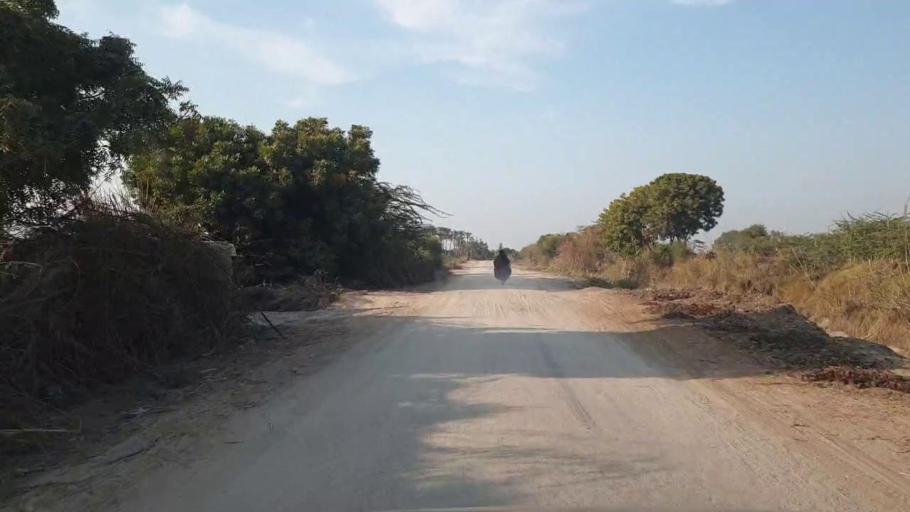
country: PK
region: Sindh
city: Shahpur Chakar
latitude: 26.1528
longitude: 68.6417
